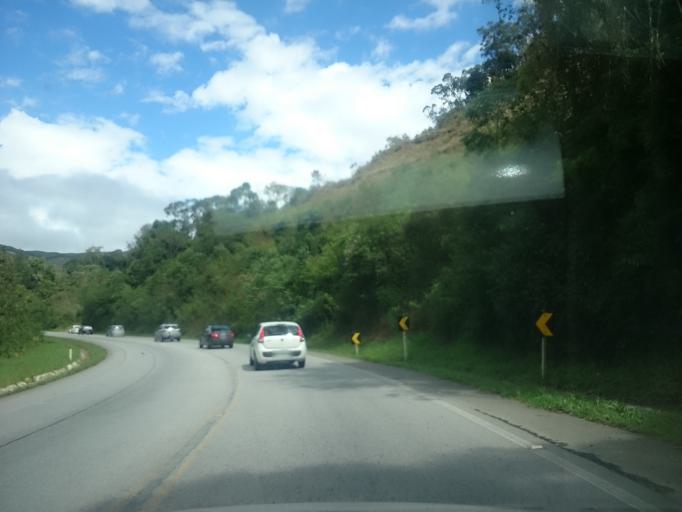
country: BR
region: Santa Catarina
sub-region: Anitapolis
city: Anitapolis
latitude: -27.6644
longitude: -49.2058
